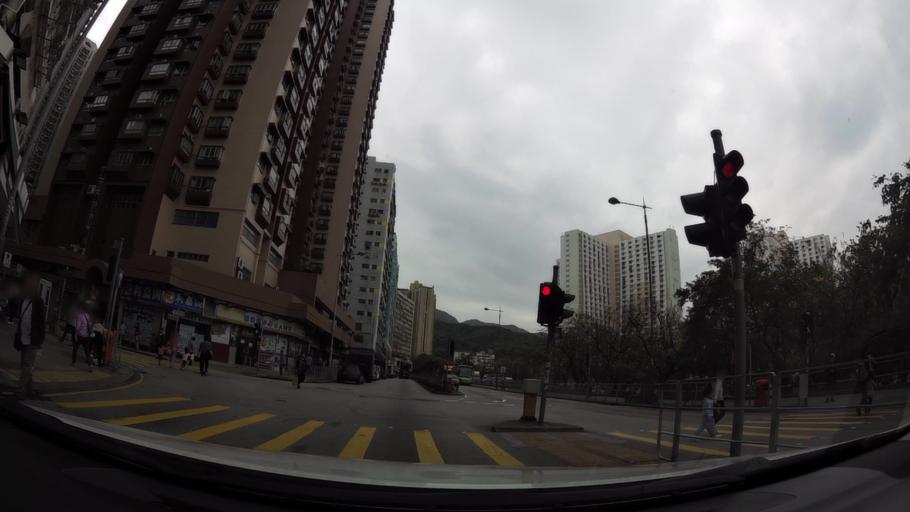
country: HK
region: Tuen Mun
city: Tuen Mun
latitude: 22.4011
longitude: 113.9715
